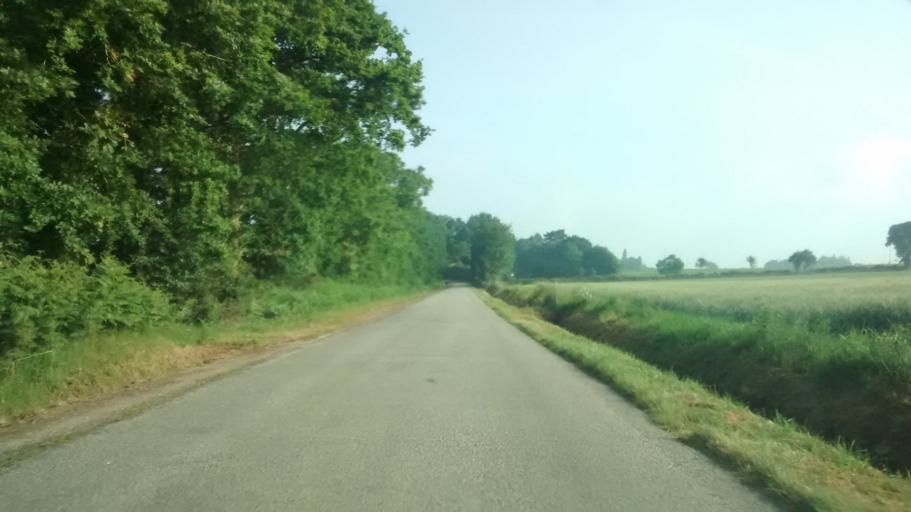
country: FR
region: Brittany
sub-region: Departement du Morbihan
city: Ruffiac
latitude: 47.8397
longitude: -2.2740
